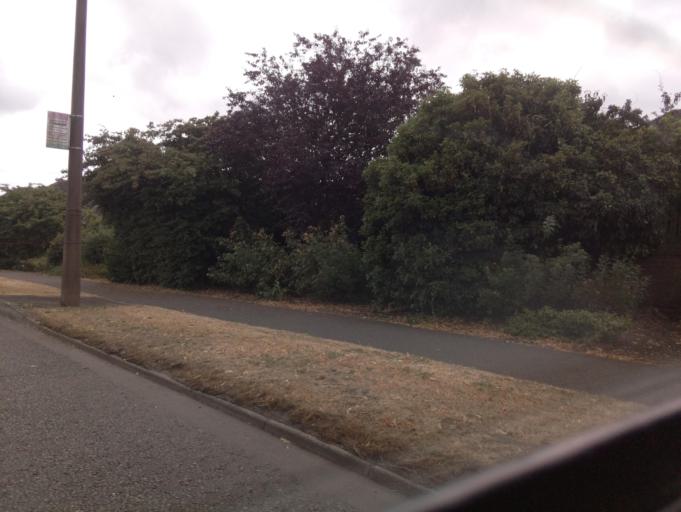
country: GB
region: England
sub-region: Derbyshire
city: Long Eaton
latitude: 52.8981
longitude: -1.2936
